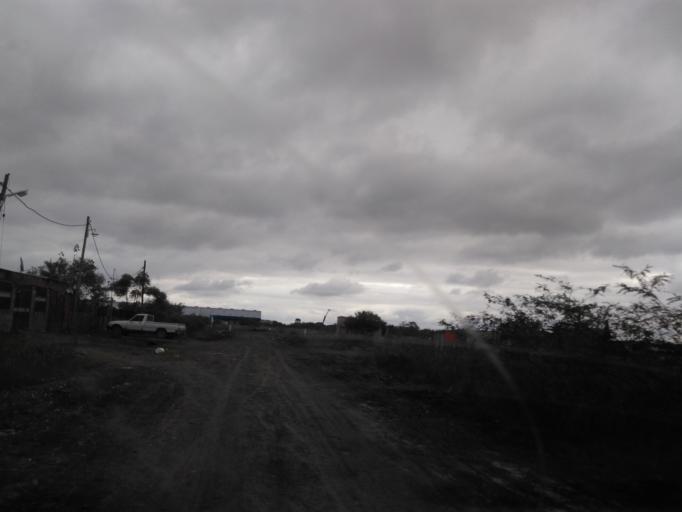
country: AR
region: Chaco
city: Fontana
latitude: -27.4610
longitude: -59.0441
